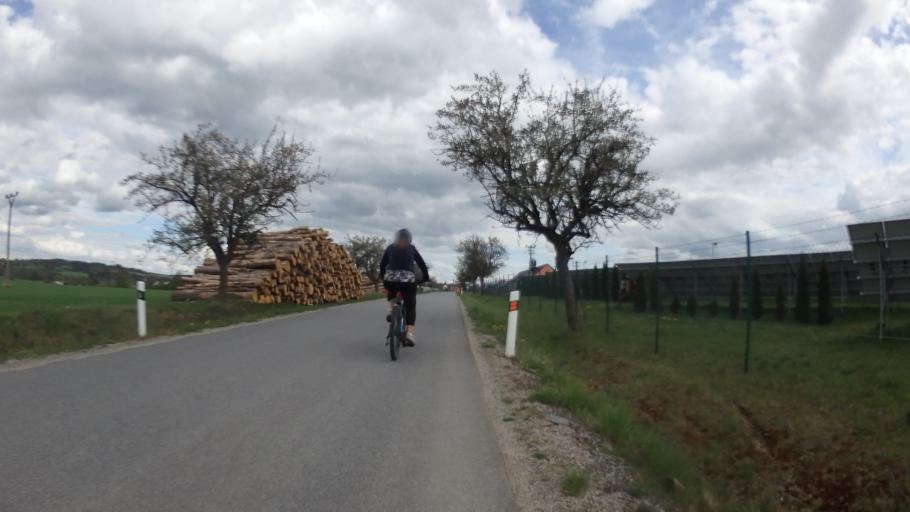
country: CZ
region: Vysocina
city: Merin
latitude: 49.3518
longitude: 15.9291
